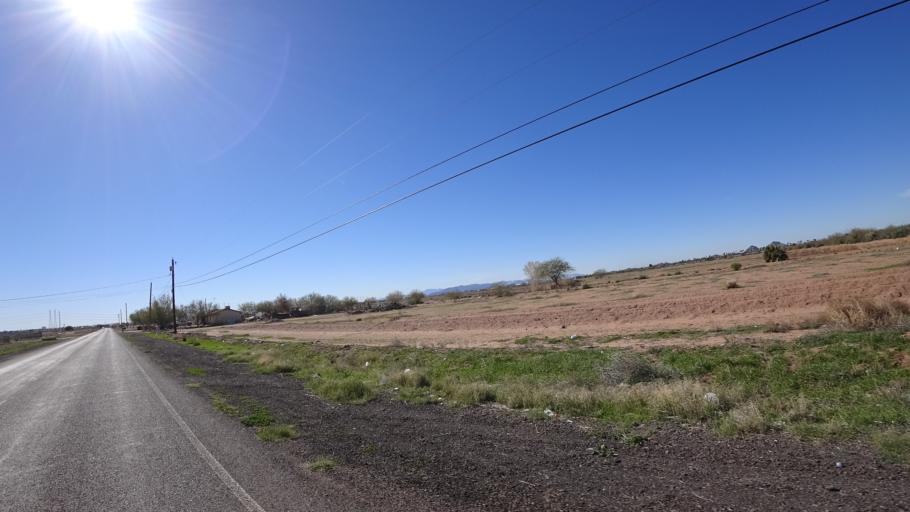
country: US
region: Arizona
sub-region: Maricopa County
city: Mesa
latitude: 33.4602
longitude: -111.8660
